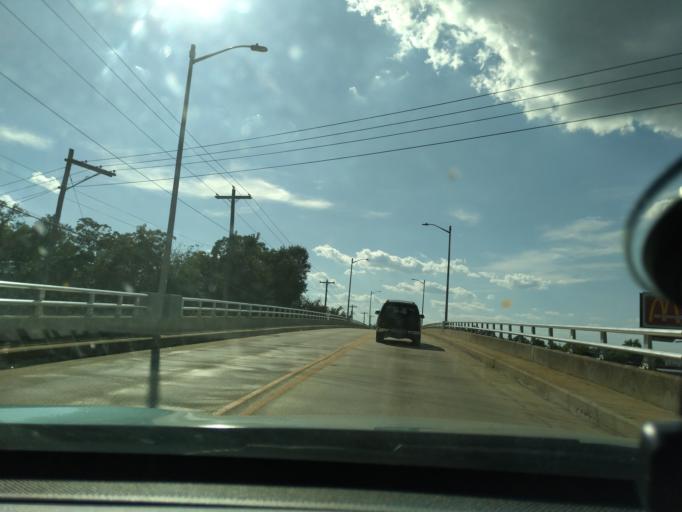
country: US
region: North Carolina
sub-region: Nash County
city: Rocky Mount
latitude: 35.9364
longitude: -77.7967
